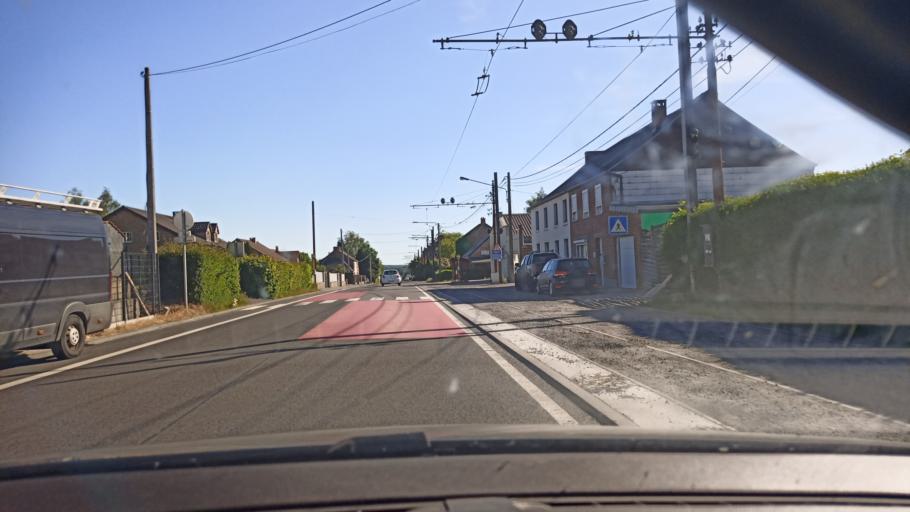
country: BE
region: Wallonia
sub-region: Province du Hainaut
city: Lobbes
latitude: 50.3581
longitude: 4.2707
